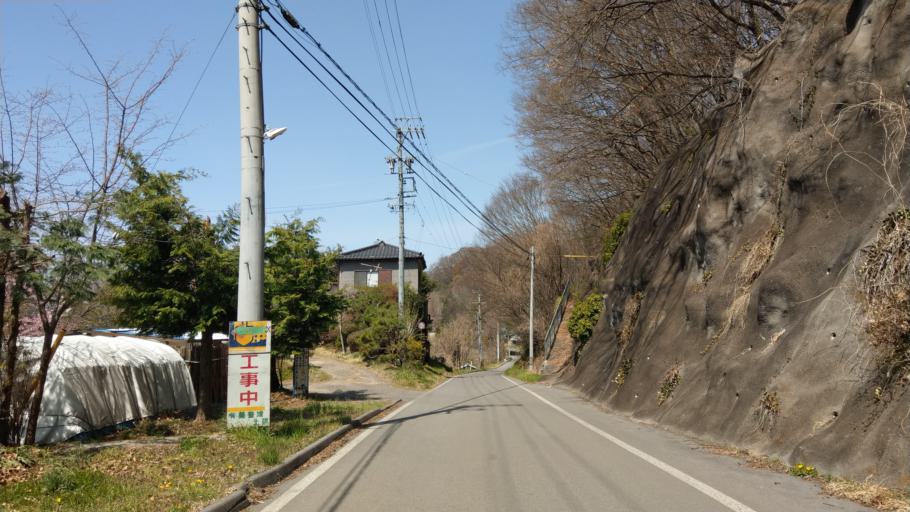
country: JP
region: Nagano
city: Komoro
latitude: 36.3355
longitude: 138.4023
